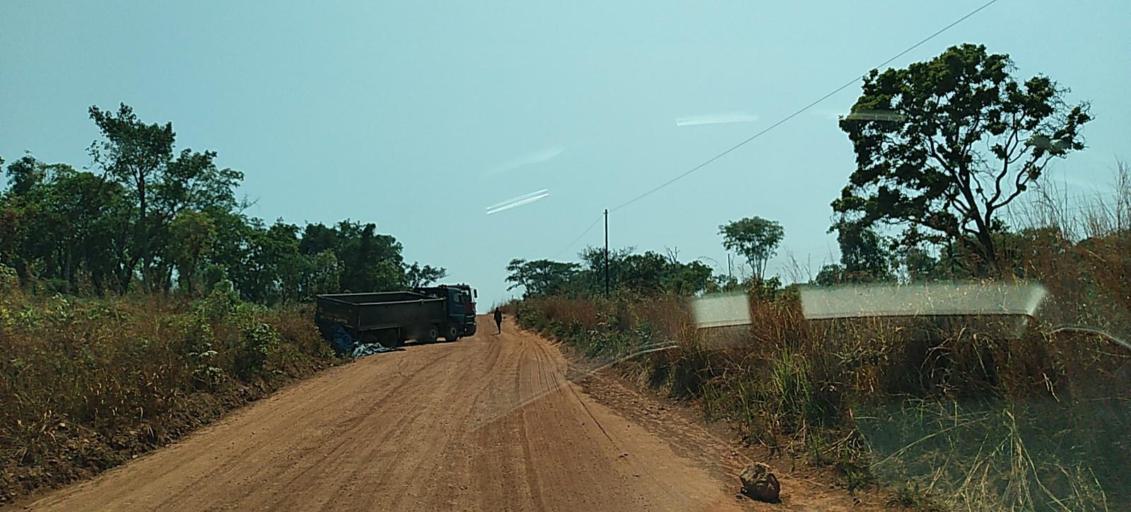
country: ZM
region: North-Western
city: Kansanshi
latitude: -12.0064
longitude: 26.5802
